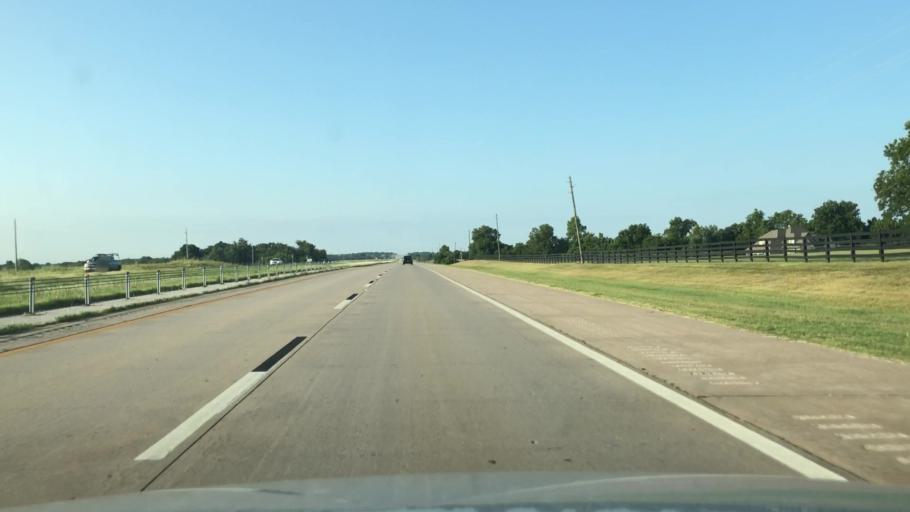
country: US
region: Oklahoma
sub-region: Osage County
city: Skiatook
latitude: 36.4644
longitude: -95.9207
